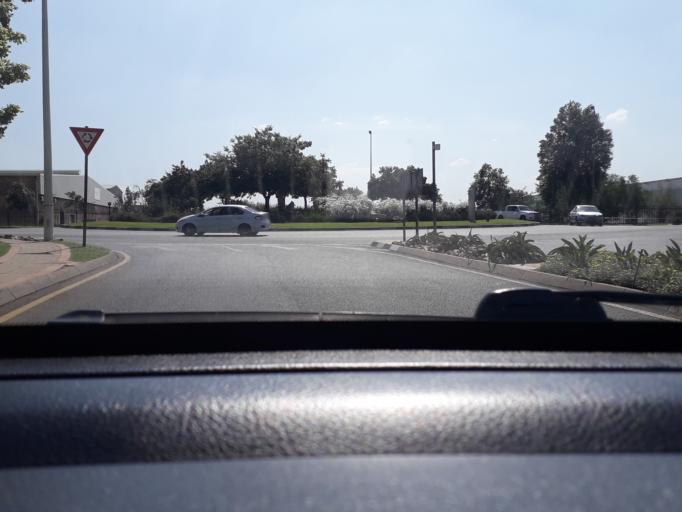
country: ZA
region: Gauteng
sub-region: City of Johannesburg Metropolitan Municipality
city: Modderfontein
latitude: -26.1121
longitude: 28.1366
